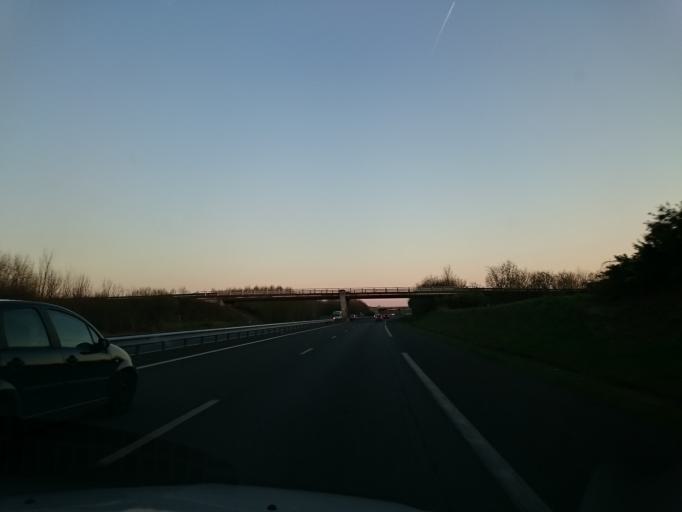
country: FR
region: Brittany
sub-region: Departement d'Ille-et-Vilaine
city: Saint-Sauveur-des-Landes
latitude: 48.3443
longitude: -1.2976
